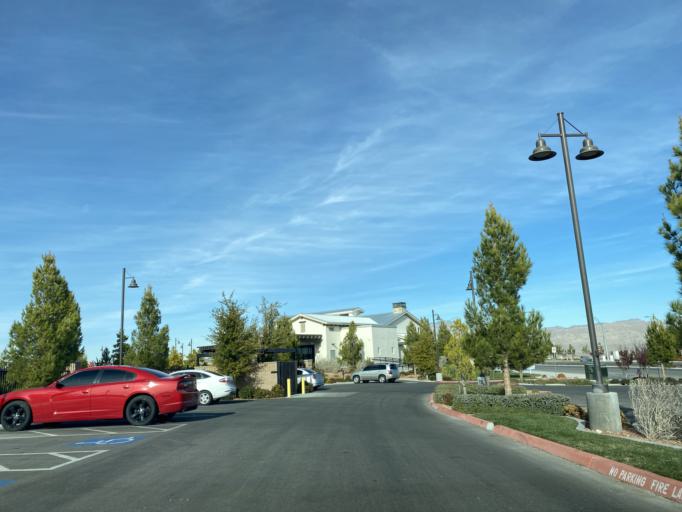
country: US
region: Nevada
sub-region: Clark County
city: Summerlin South
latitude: 36.3129
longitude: -115.3155
